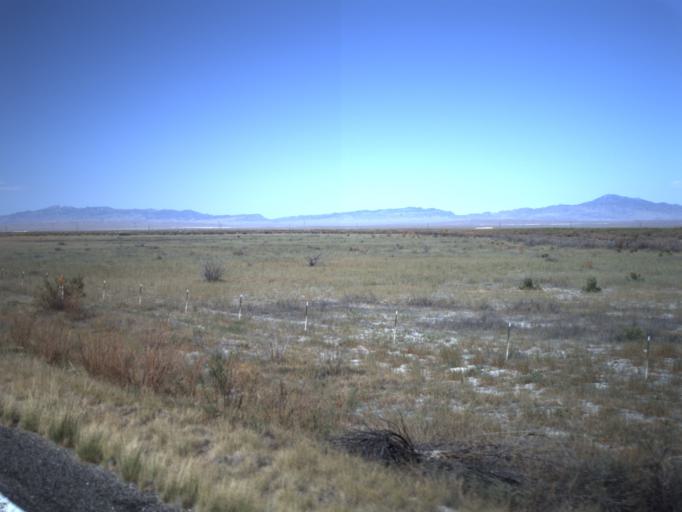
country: US
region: Utah
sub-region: Millard County
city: Delta
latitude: 39.2779
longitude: -112.8501
